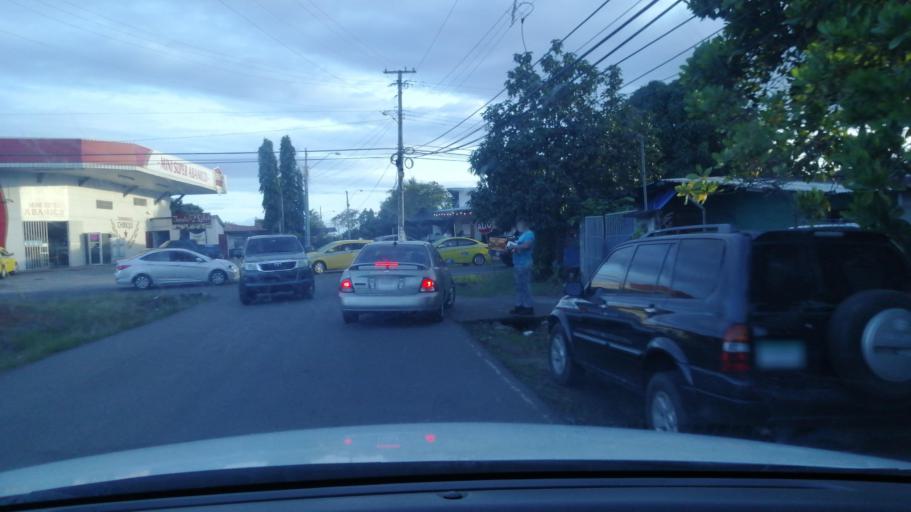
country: PA
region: Chiriqui
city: David
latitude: 8.4021
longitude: -82.4358
